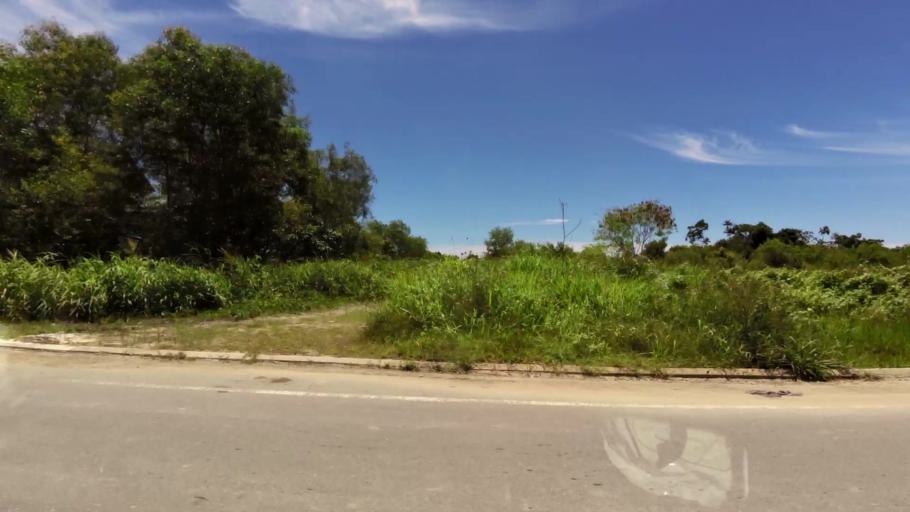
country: BN
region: Brunei and Muara
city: Bandar Seri Begawan
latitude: 5.0231
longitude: 115.0337
